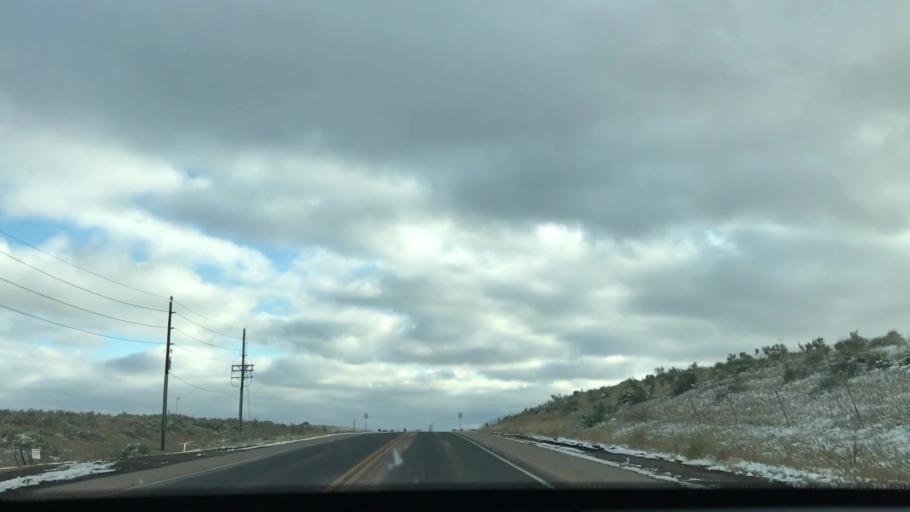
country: US
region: Colorado
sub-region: Boulder County
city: Lafayette
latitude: 39.9699
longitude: -105.0719
